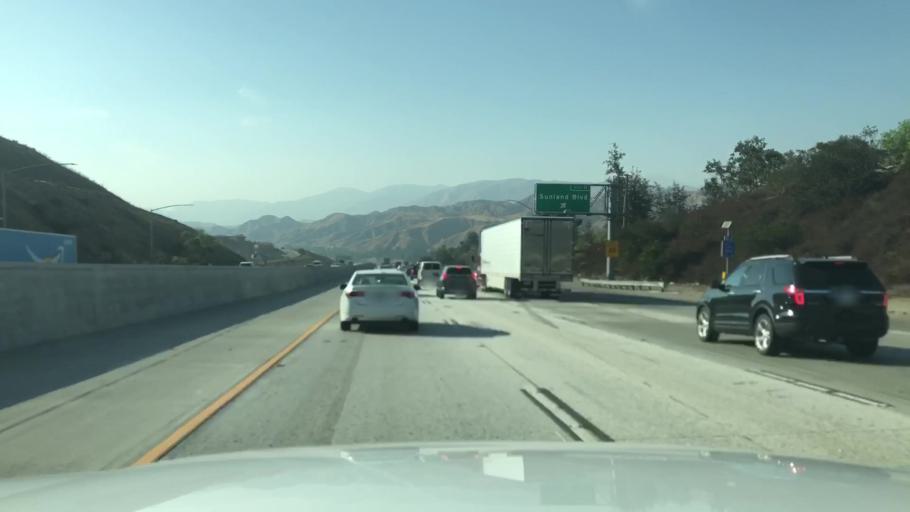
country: US
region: California
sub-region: Los Angeles County
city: Burbank
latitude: 34.2556
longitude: -118.3244
